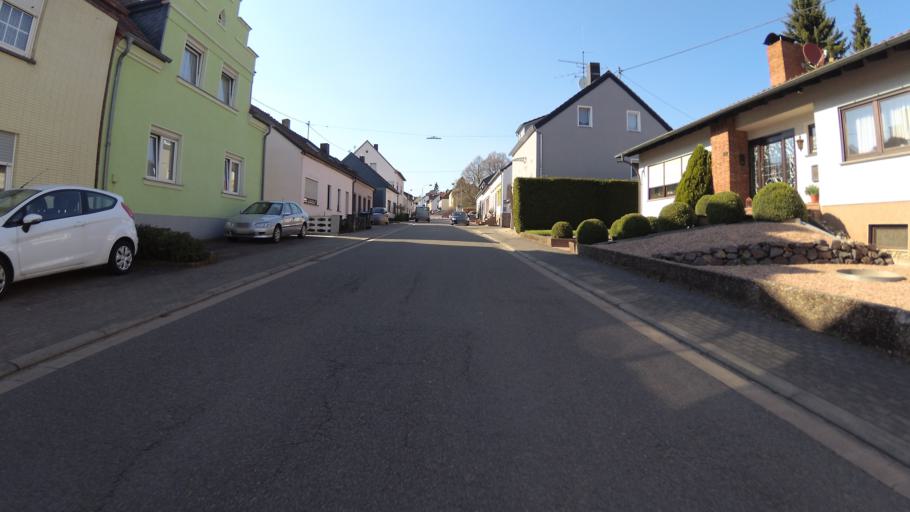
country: DE
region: Saarland
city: Merchweiler
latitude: 49.3558
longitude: 7.0625
